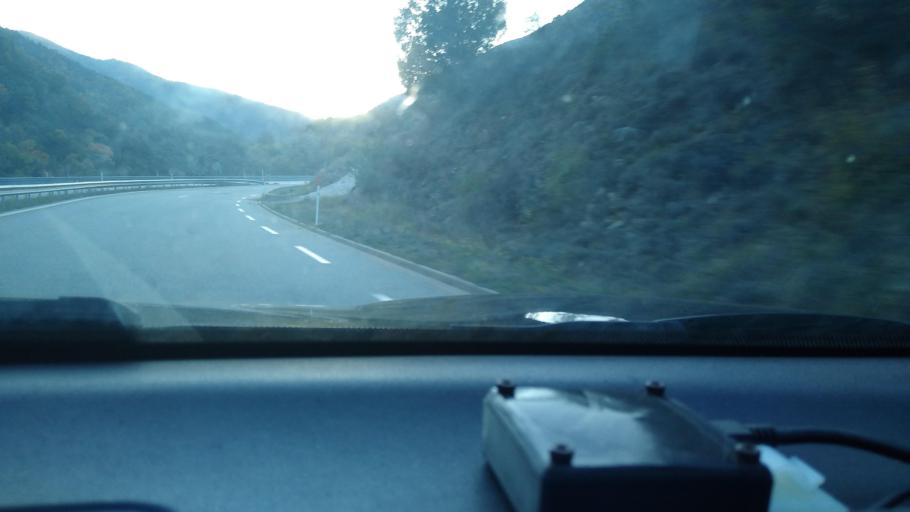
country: FR
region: Languedoc-Roussillon
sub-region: Departement des Pyrenees-Orientales
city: Vernet-les-Bains
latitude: 42.5171
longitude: 2.2005
